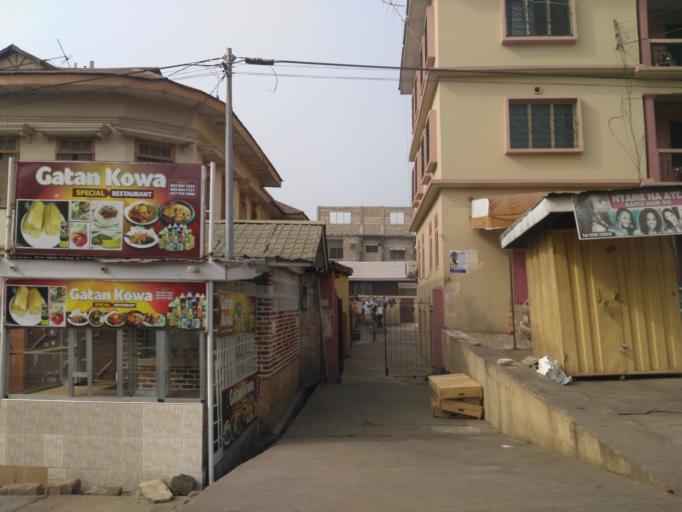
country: GH
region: Ashanti
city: Kumasi
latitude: 6.6993
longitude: -1.6089
